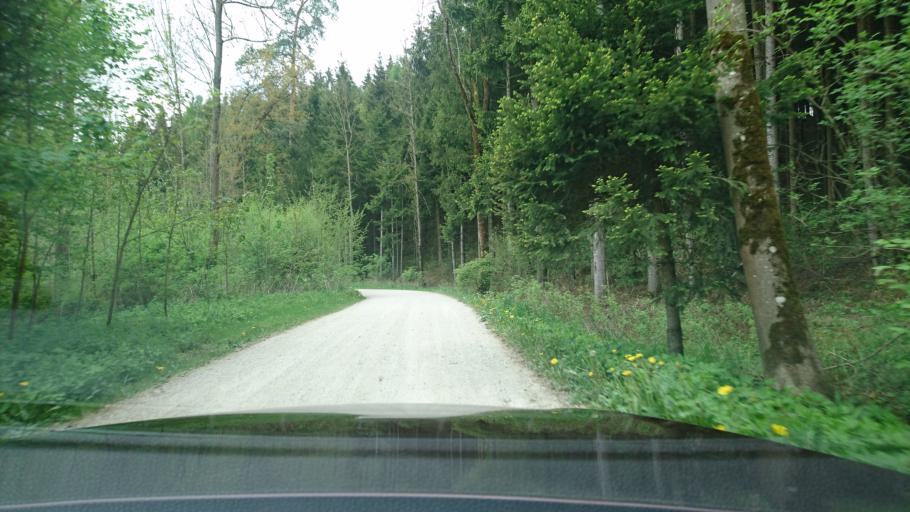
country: DE
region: Bavaria
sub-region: Lower Bavaria
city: Stallwang
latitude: 48.5367
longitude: 12.2214
